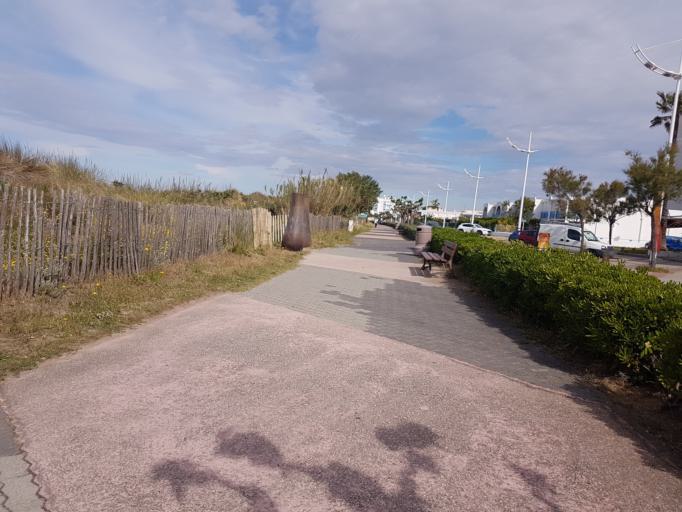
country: FR
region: Languedoc-Roussillon
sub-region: Departement du Gard
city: Le Grau-du-Roi
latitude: 43.5451
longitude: 4.1270
